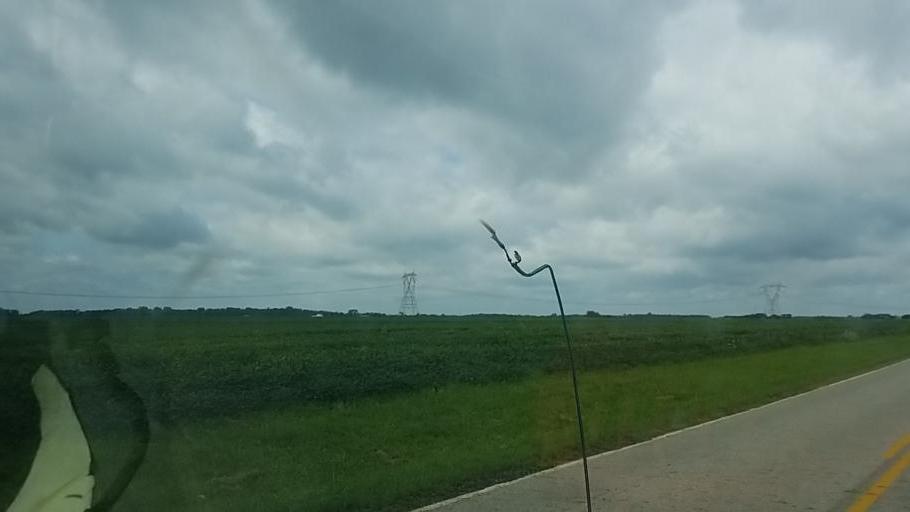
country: US
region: Ohio
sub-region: Madison County
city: Mount Sterling
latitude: 39.7762
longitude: -83.2174
